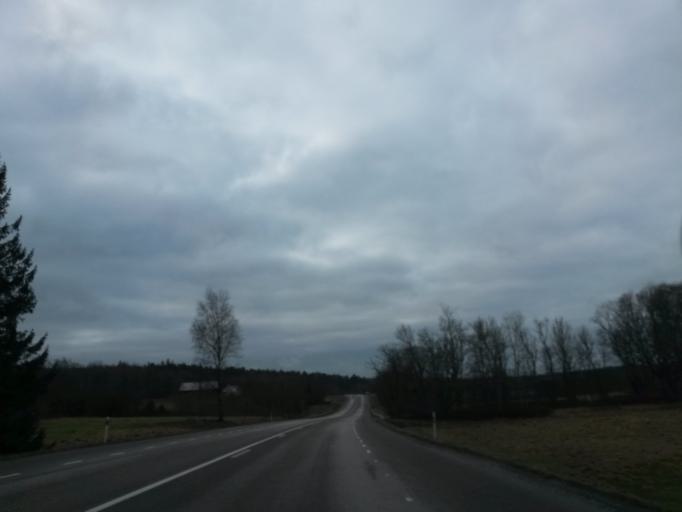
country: SE
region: Vaestra Goetaland
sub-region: Alingsas Kommun
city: Alingsas
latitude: 57.9394
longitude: 12.5858
